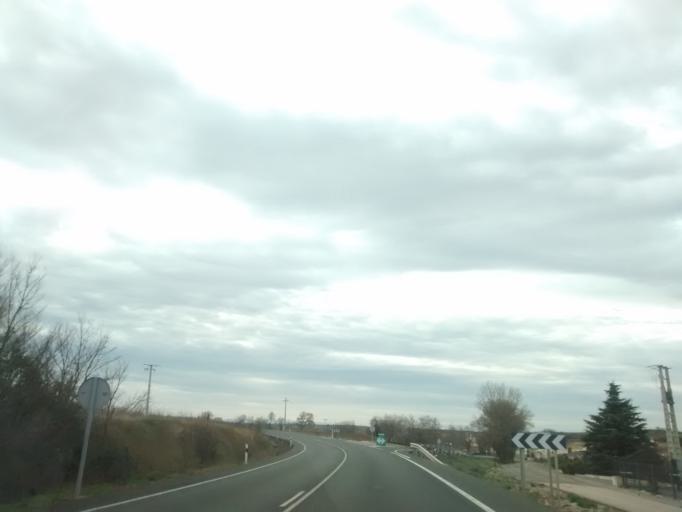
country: ES
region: La Rioja
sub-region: Provincia de La Rioja
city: Gimileo
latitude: 42.5489
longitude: -2.8160
